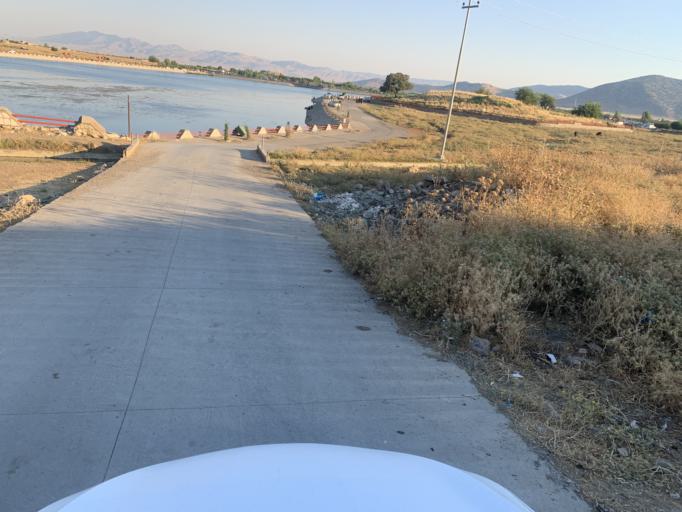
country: IQ
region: As Sulaymaniyah
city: Raniye
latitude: 36.2757
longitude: 44.7541
